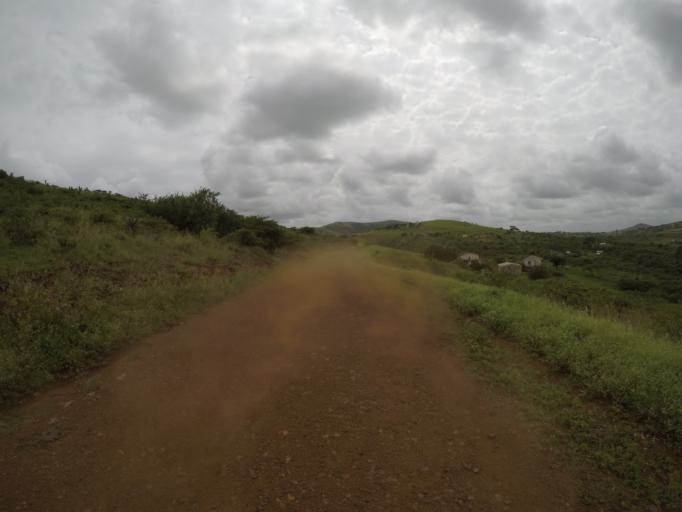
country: ZA
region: KwaZulu-Natal
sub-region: uThungulu District Municipality
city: Empangeni
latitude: -28.6236
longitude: 31.8902
